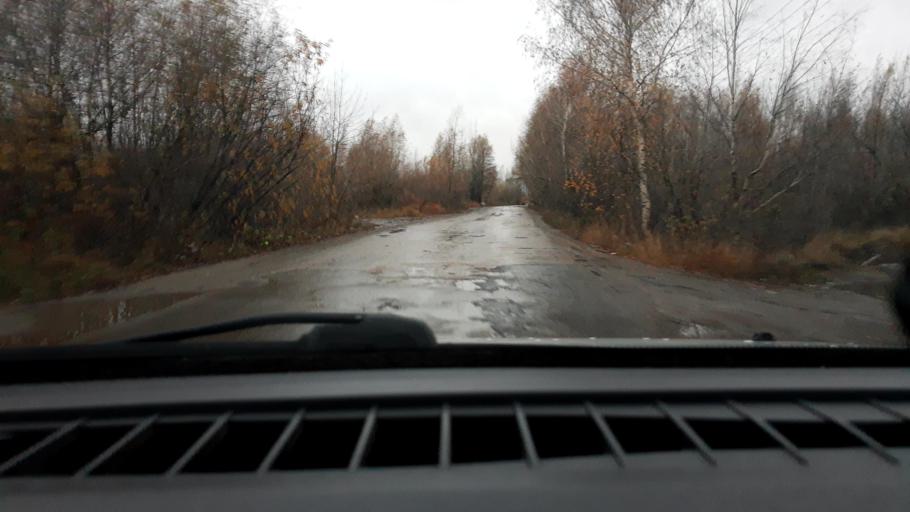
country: RU
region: Nizjnij Novgorod
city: Gorbatovka
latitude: 56.2673
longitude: 43.8582
